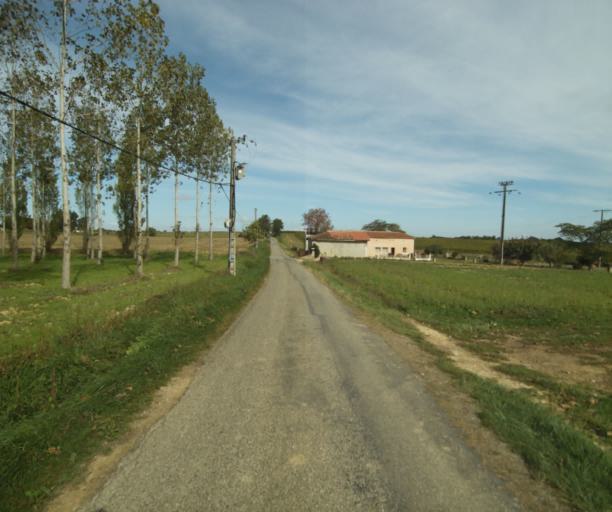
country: FR
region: Midi-Pyrenees
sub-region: Departement du Gers
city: Eauze
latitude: 43.8492
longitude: 0.1400
